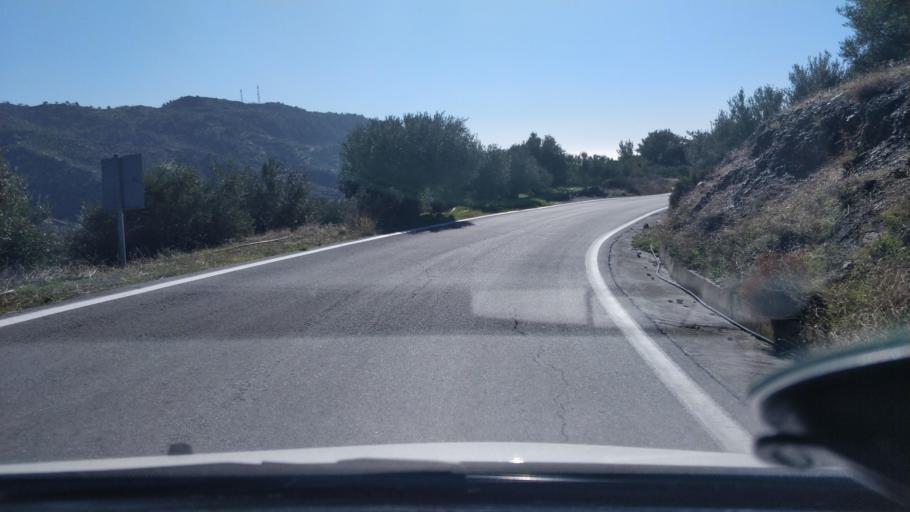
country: GR
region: Crete
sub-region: Nomos Irakleiou
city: Kastelli
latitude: 35.0306
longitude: 25.4491
